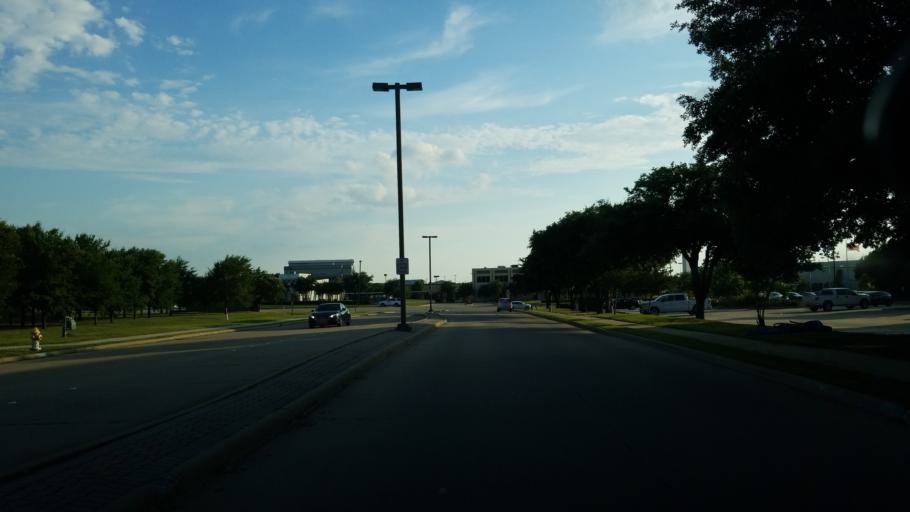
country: US
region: Texas
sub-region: Dallas County
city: Farmers Branch
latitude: 32.9109
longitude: -96.9539
